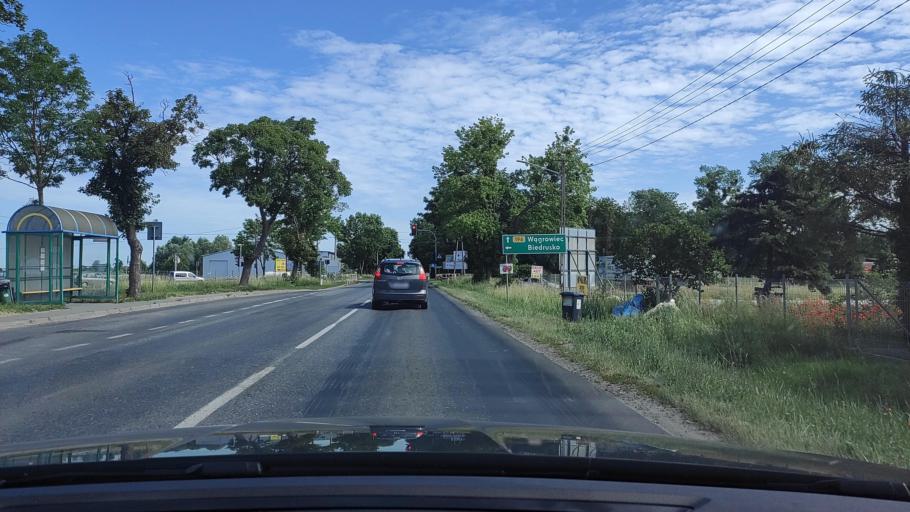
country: PL
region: Greater Poland Voivodeship
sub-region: Powiat poznanski
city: Murowana Goslina
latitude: 52.5424
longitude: 16.9865
